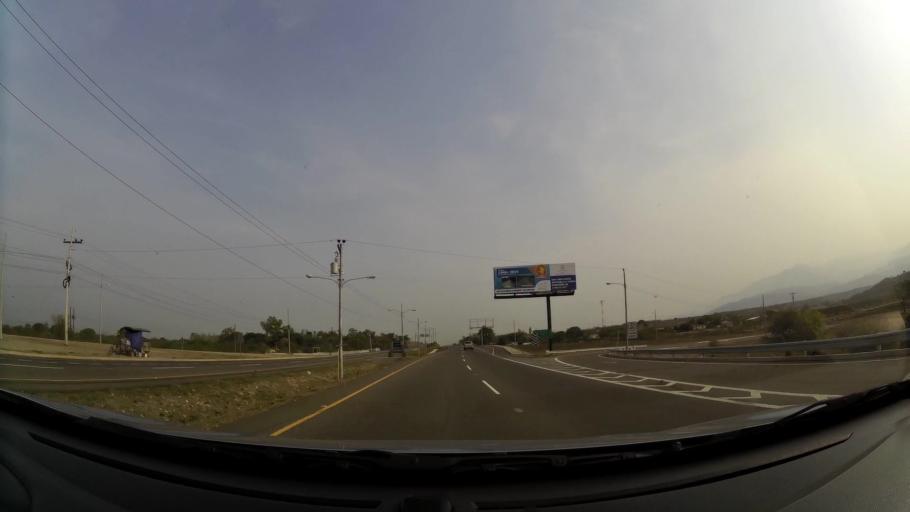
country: HN
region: Comayagua
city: Villa de San Antonio
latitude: 14.3488
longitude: -87.5959
